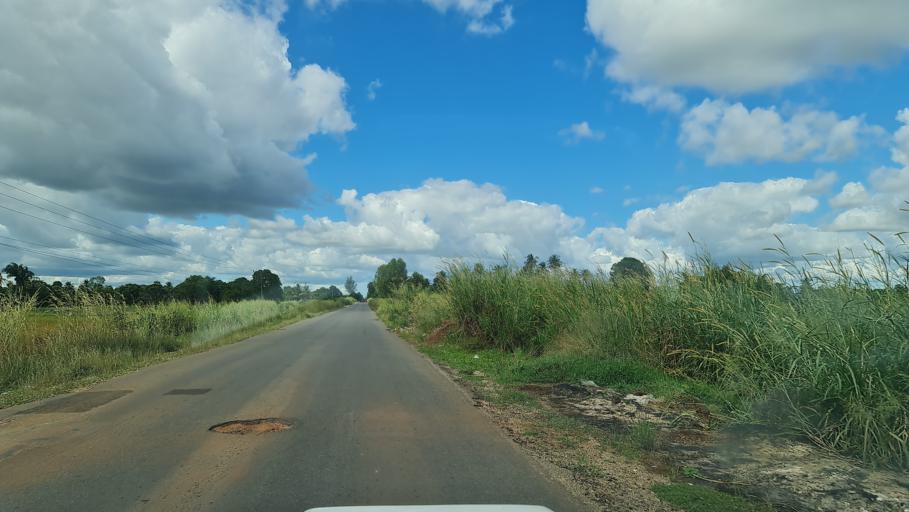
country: MZ
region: Zambezia
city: Quelimane
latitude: -17.5958
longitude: 36.7839
